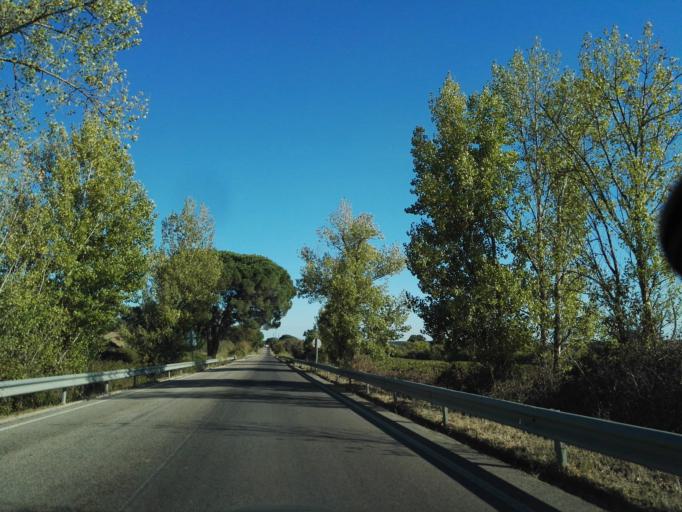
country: PT
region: Santarem
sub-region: Benavente
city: Poceirao
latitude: 38.8544
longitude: -8.7261
